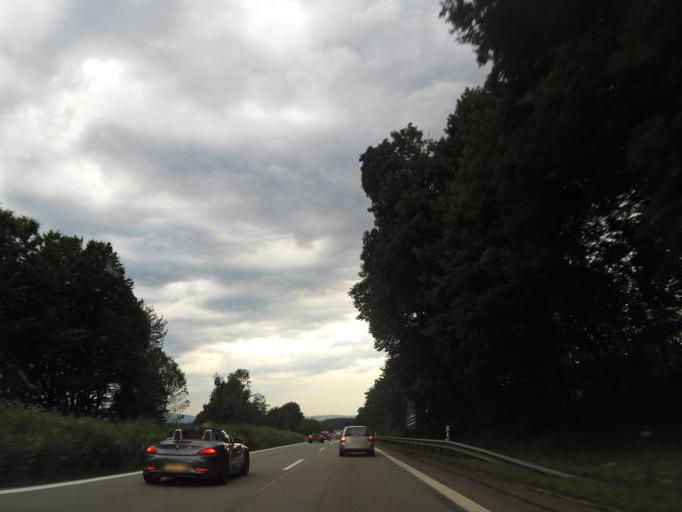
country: DE
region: Bavaria
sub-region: Upper Bavaria
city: Rohrdorf
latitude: 47.8031
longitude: 12.1673
